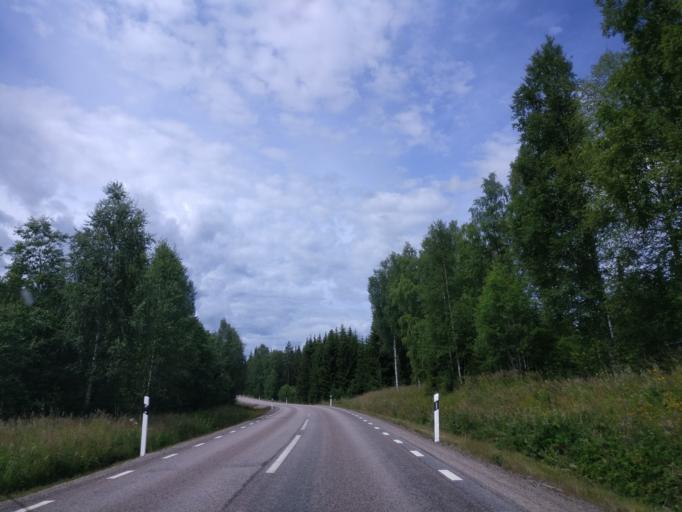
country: SE
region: Vaermland
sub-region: Hagfors Kommun
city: Ekshaerad
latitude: 60.1794
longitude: 13.3799
